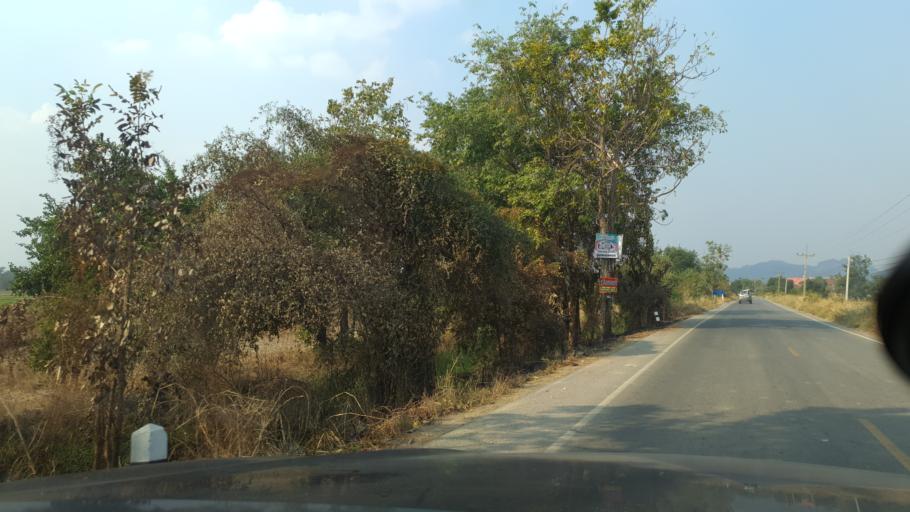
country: TH
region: Sukhothai
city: Ban Dan Lan Hoi
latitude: 17.1069
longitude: 99.5508
